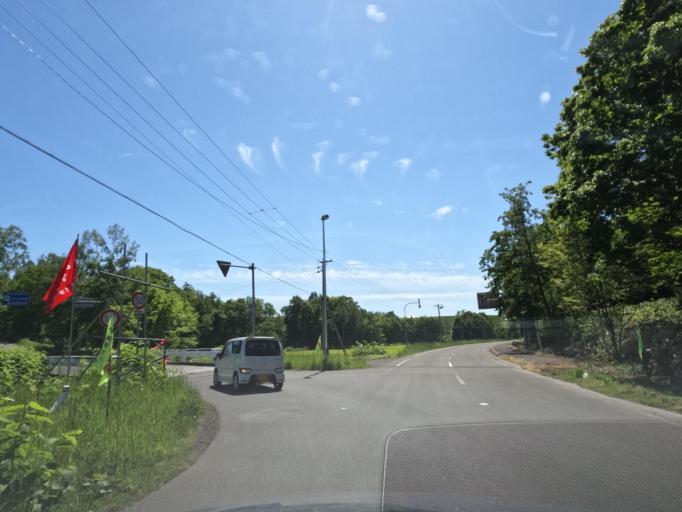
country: JP
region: Hokkaido
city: Iwamizawa
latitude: 43.0965
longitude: 141.7646
